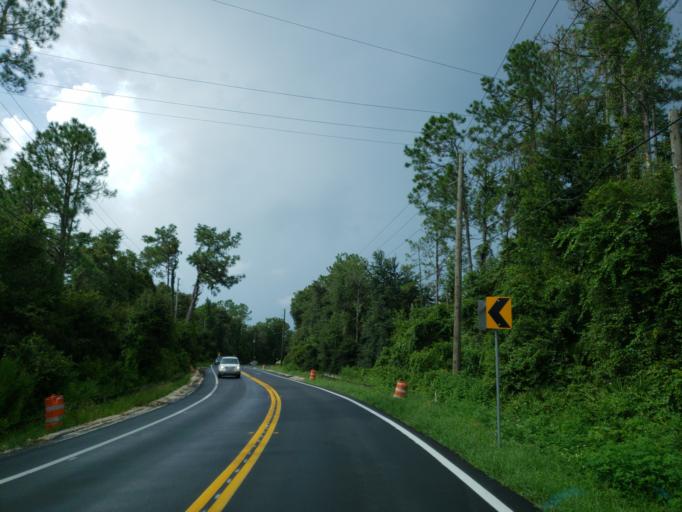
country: US
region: Florida
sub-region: Pasco County
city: Land O' Lakes
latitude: 28.2554
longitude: -82.4491
